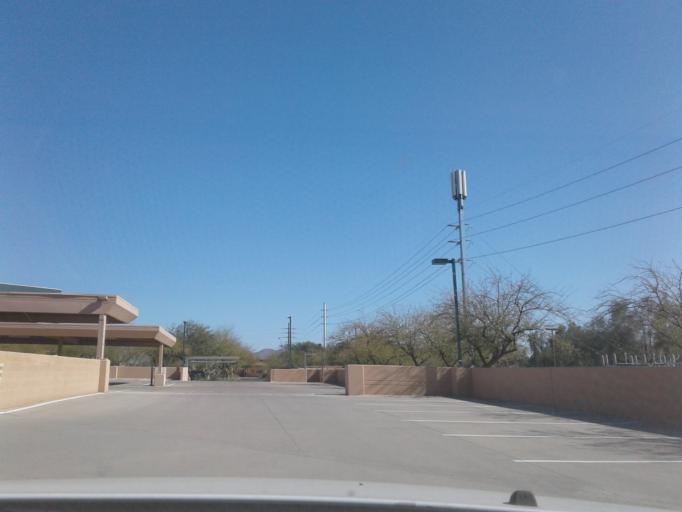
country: US
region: Arizona
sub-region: Maricopa County
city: Paradise Valley
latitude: 33.6187
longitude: -111.9278
